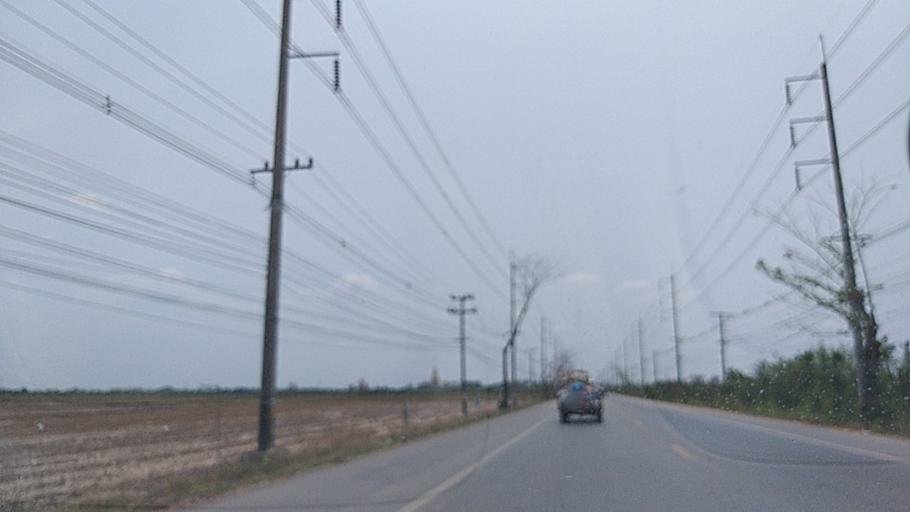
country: TH
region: Chachoengsao
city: Bang Nam Priao
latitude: 13.8140
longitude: 101.0535
